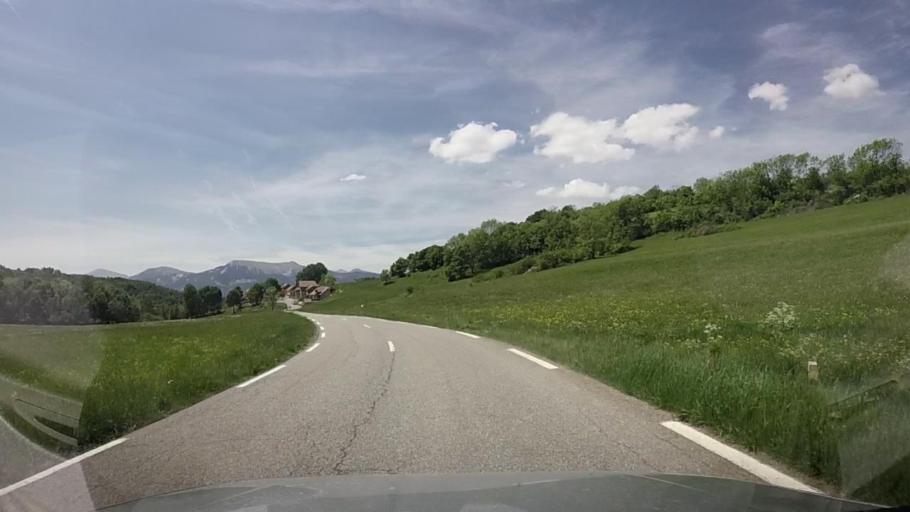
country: FR
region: Provence-Alpes-Cote d'Azur
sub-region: Departement des Alpes-de-Haute-Provence
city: Seyne-les-Alpes
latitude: 44.4151
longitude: 6.3489
